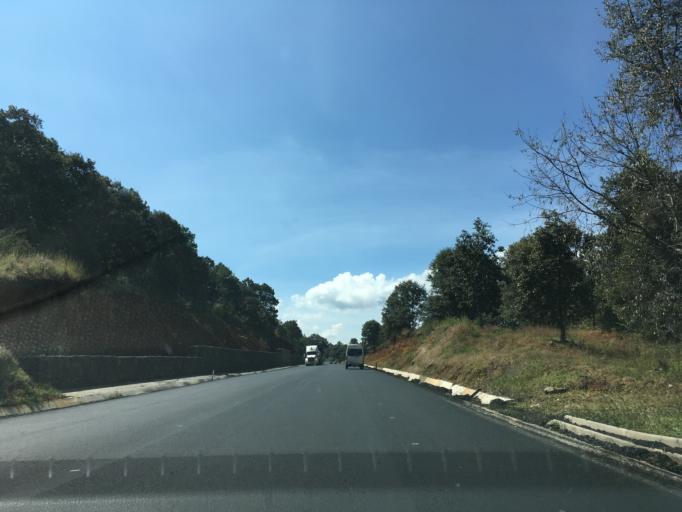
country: MX
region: Michoacan
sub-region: Patzcuaro
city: Santa Ana Chapitiro
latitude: 19.5053
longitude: -101.6834
